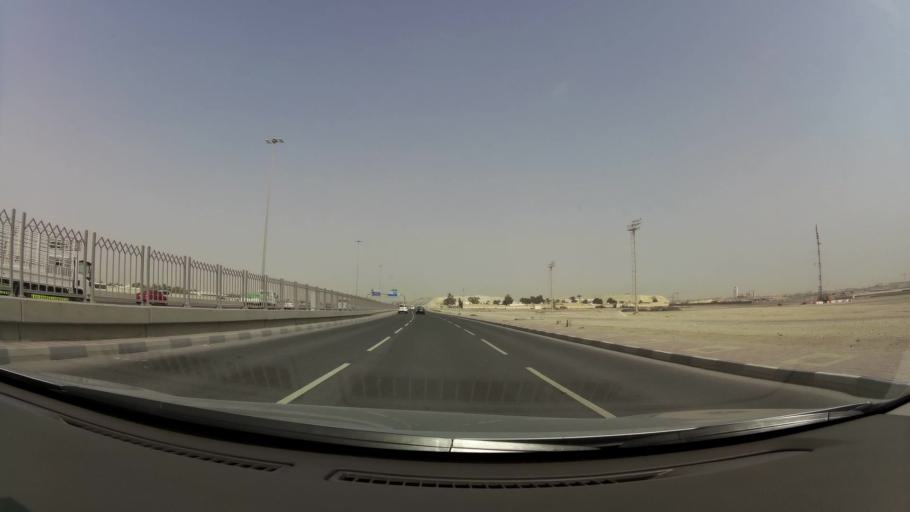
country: QA
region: Baladiyat ad Dawhah
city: Doha
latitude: 25.2819
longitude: 51.4851
